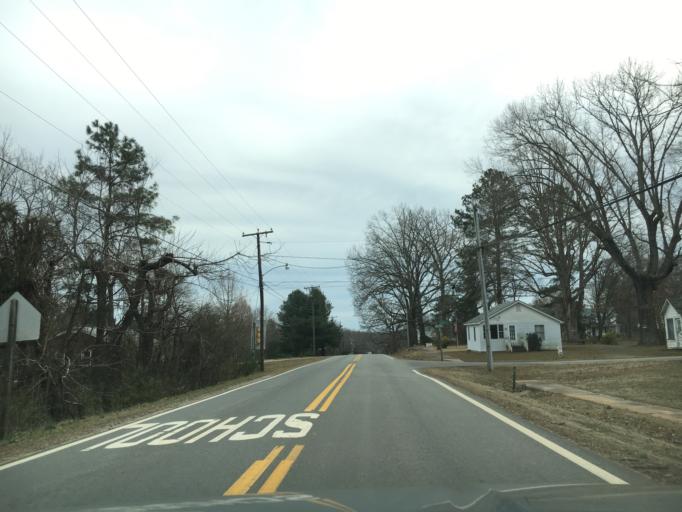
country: US
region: Virginia
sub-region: Charlotte County
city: Charlotte Court House
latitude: 37.0839
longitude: -78.7463
